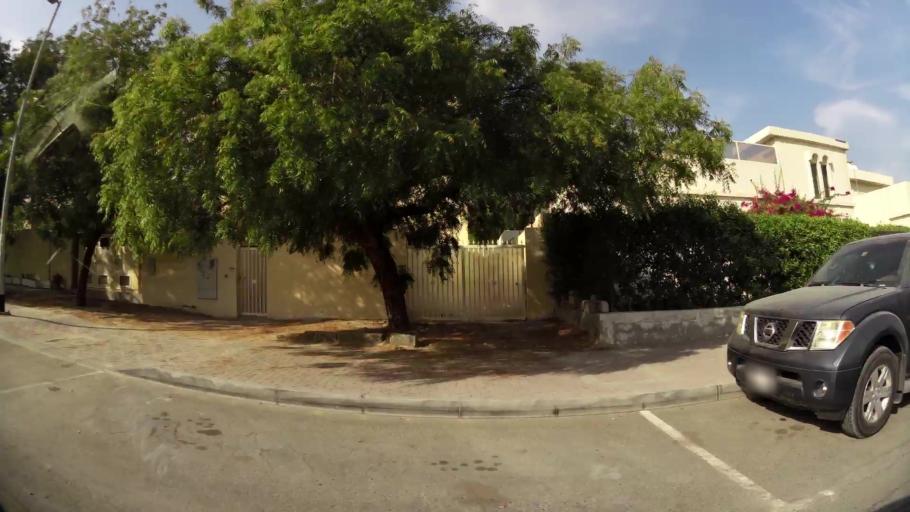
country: AE
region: Ash Shariqah
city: Sharjah
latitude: 25.2214
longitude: 55.3810
